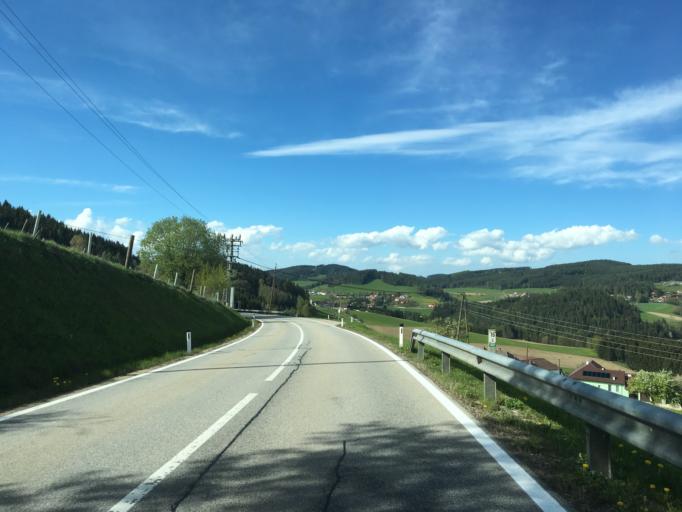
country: AT
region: Upper Austria
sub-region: Politischer Bezirk Urfahr-Umgebung
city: Haibach im Muhlkreis
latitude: 48.4345
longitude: 14.3587
